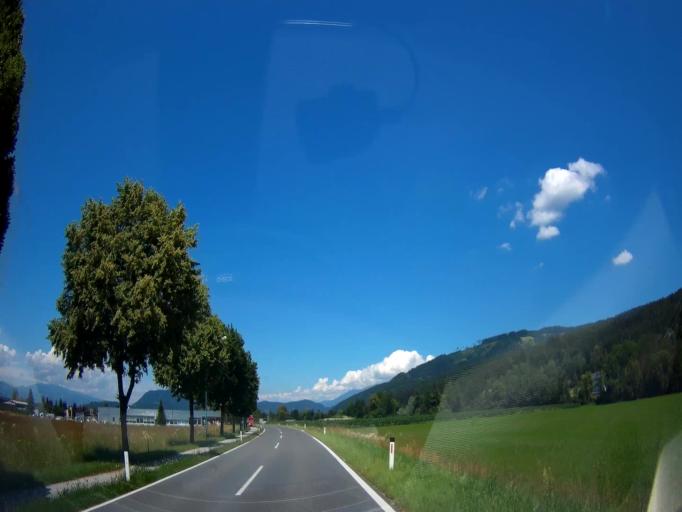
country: AT
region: Carinthia
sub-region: Politischer Bezirk Volkermarkt
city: Bleiburg/Pliberk
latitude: 46.5956
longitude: 14.7968
